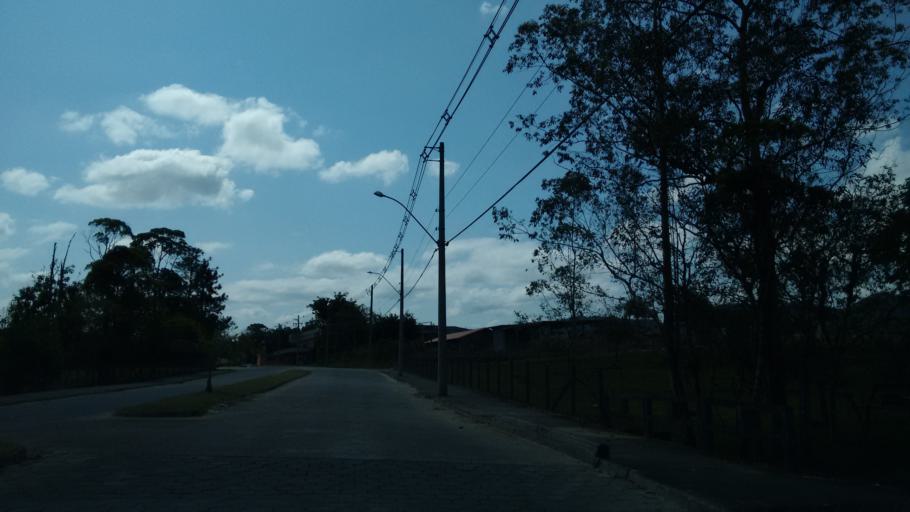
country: BR
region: Santa Catarina
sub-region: Pomerode
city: Pomerode
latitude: -26.7545
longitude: -49.1749
